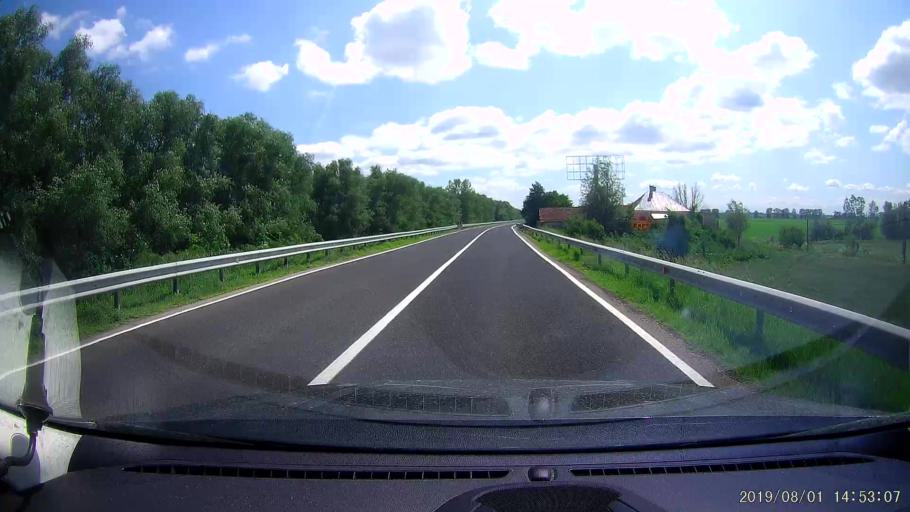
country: RO
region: Braila
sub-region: Comuna Vadeni
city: Vadeni
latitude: 45.3423
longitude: 28.0065
